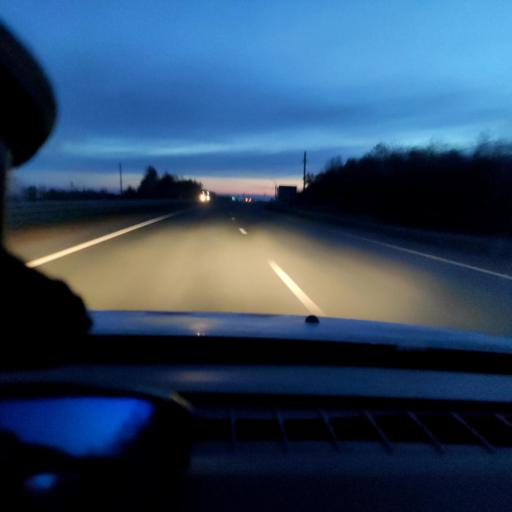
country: RU
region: Samara
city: Novokuybyshevsk
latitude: 53.0010
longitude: 49.9609
